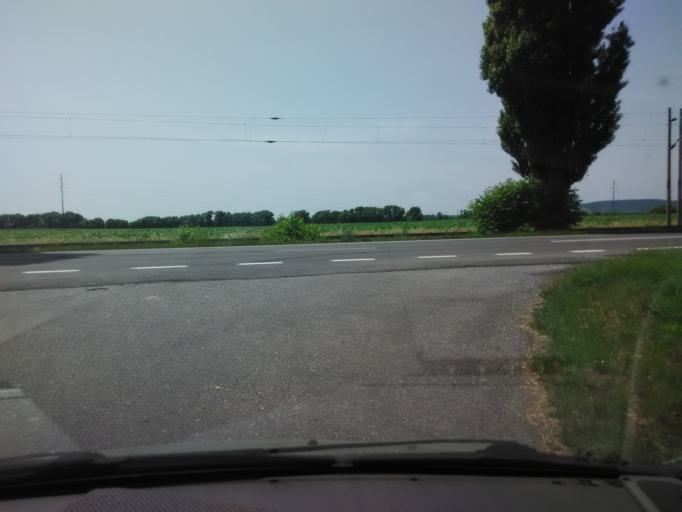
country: SK
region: Nitriansky
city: Tlmace
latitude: 48.2607
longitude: 18.5715
